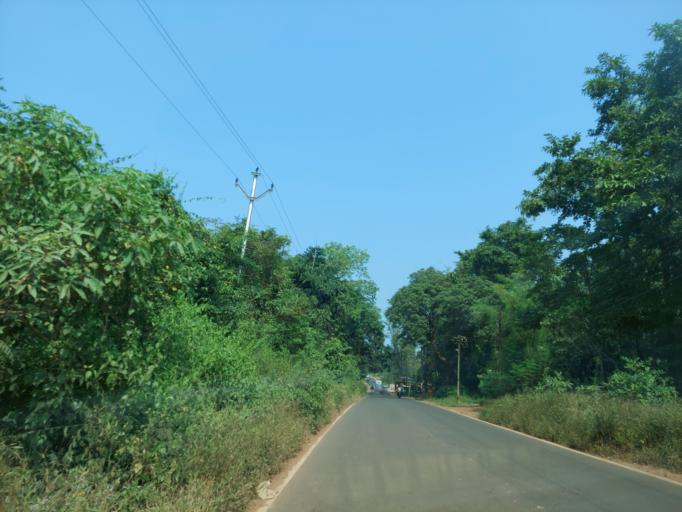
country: IN
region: Maharashtra
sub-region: Sindhudurg
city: Kudal
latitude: 15.9918
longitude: 73.6840
